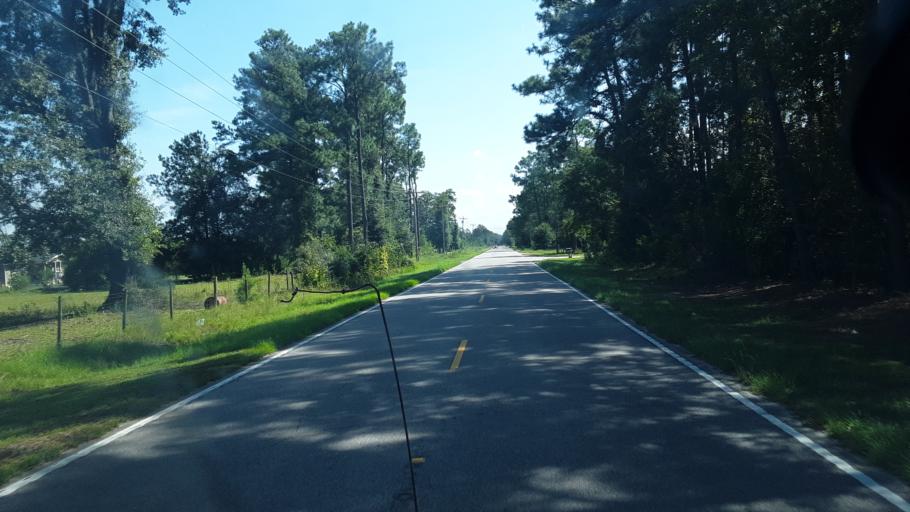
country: US
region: South Carolina
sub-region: Hampton County
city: Varnville
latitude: 32.8785
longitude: -81.0373
